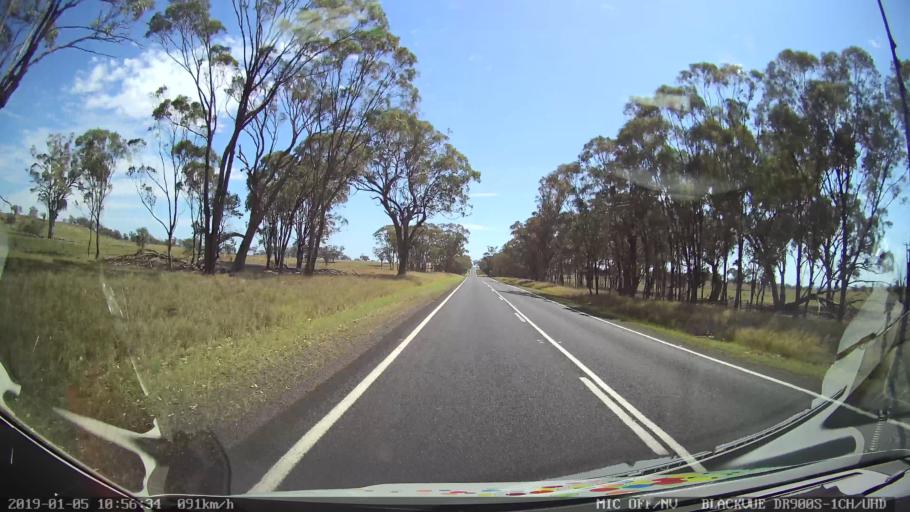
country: AU
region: New South Wales
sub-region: Warrumbungle Shire
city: Coonabarabran
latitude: -31.4401
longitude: 149.1596
